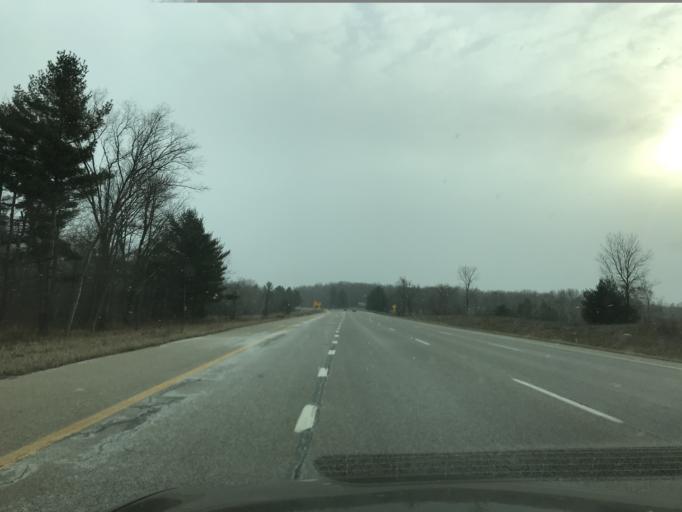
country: US
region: Michigan
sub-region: Clare County
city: Clare
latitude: 43.8563
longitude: -84.7789
